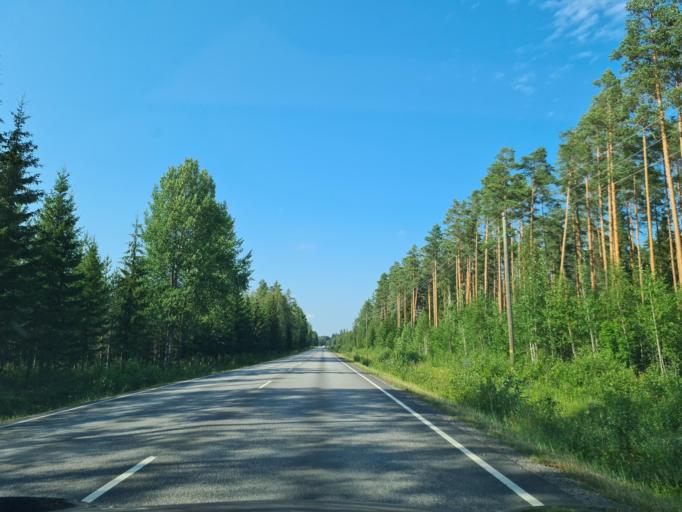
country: FI
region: Satakunta
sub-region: Pohjois-Satakunta
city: Kankaanpaeae
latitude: 61.9261
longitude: 22.5076
